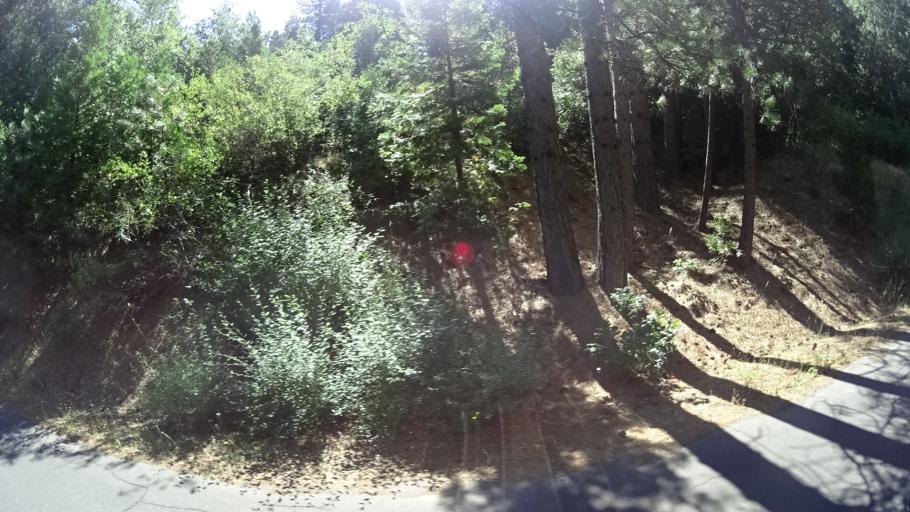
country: US
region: California
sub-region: Calaveras County
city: Arnold
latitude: 38.2549
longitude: -120.3666
